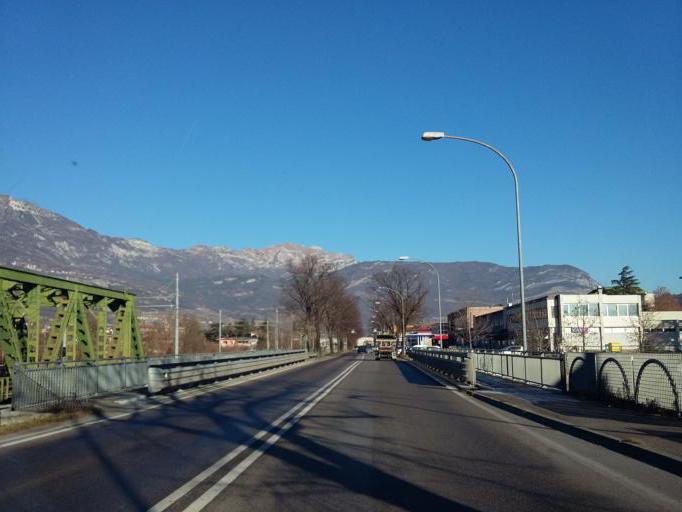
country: IT
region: Trentino-Alto Adige
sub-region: Provincia di Trento
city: Rovereto
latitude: 45.8830
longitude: 11.0325
